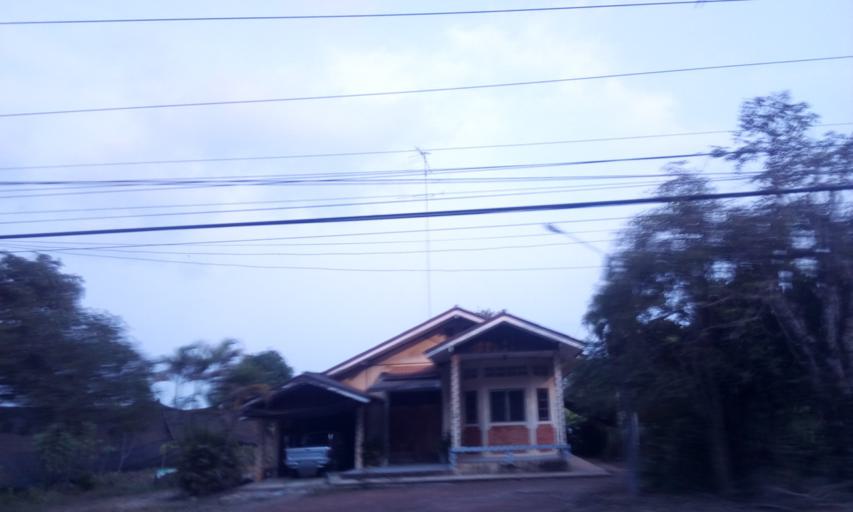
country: TH
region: Trat
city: Khao Saming
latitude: 12.3570
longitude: 102.3823
